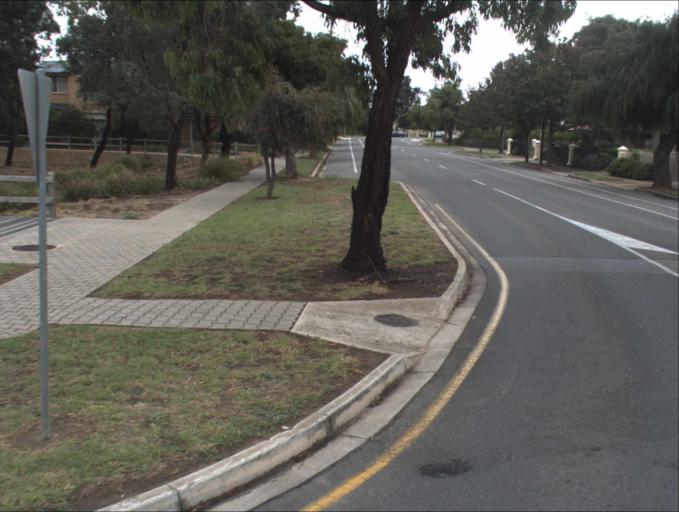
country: AU
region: South Australia
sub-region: Charles Sturt
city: Woodville North
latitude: -34.8682
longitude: 138.5584
